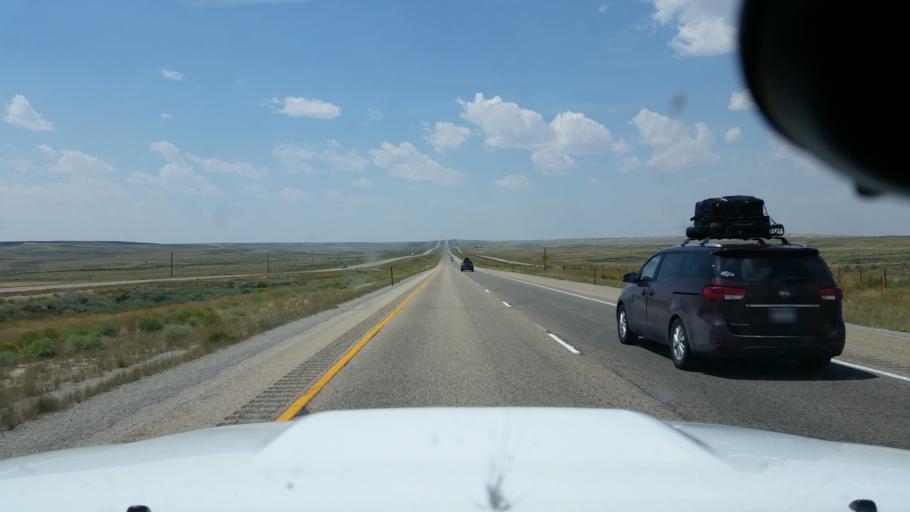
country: US
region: Wyoming
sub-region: Carbon County
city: Rawlins
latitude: 41.7471
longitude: -107.5937
